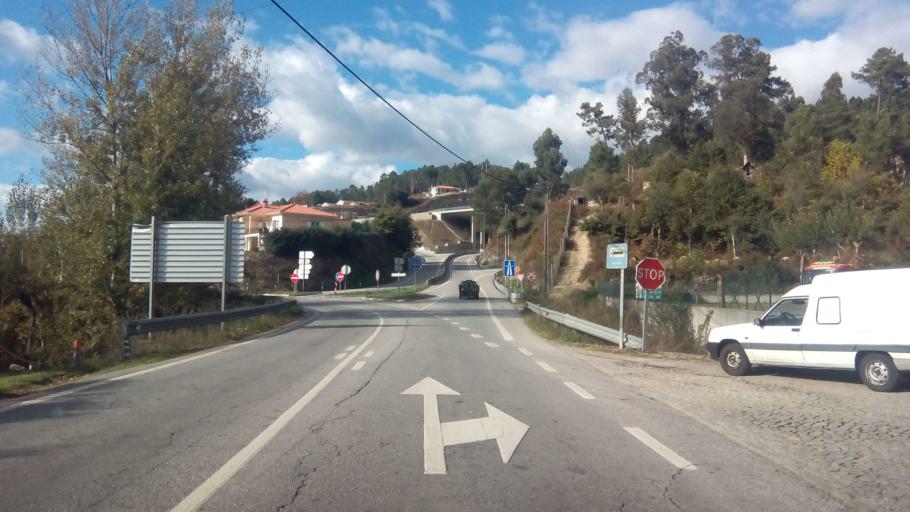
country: PT
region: Porto
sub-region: Amarante
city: Amarante
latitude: 41.2534
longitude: -8.0451
